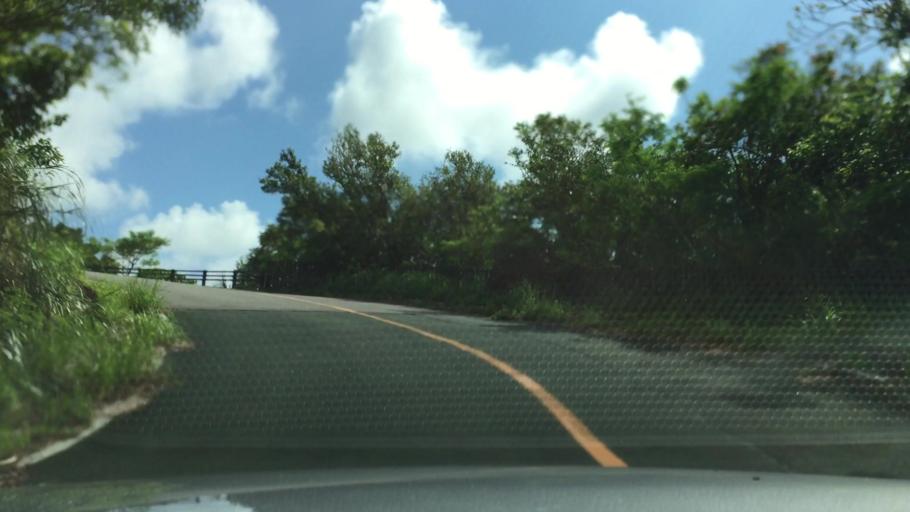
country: JP
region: Okinawa
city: Ishigaki
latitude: 24.3781
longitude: 124.1646
